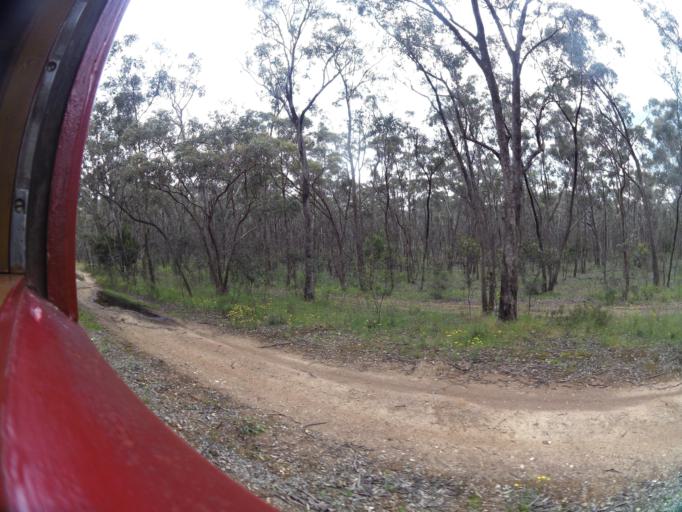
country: AU
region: Victoria
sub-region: Mount Alexander
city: Castlemaine
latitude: -37.0059
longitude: 144.1173
